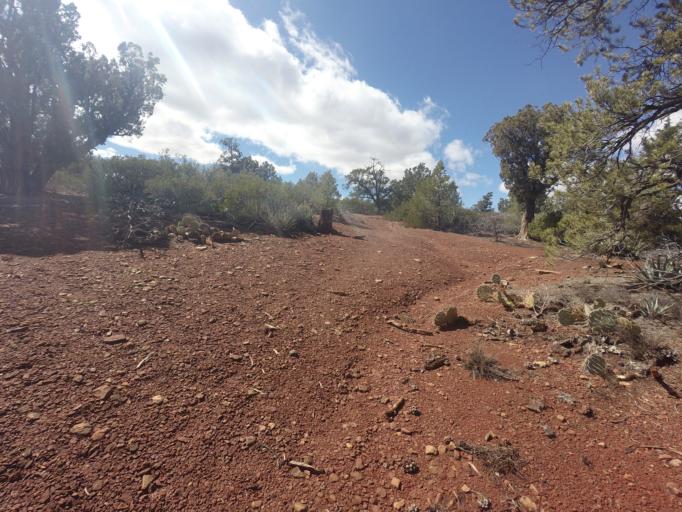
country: US
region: Arizona
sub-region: Yavapai County
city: West Sedona
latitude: 34.8962
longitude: -111.8202
